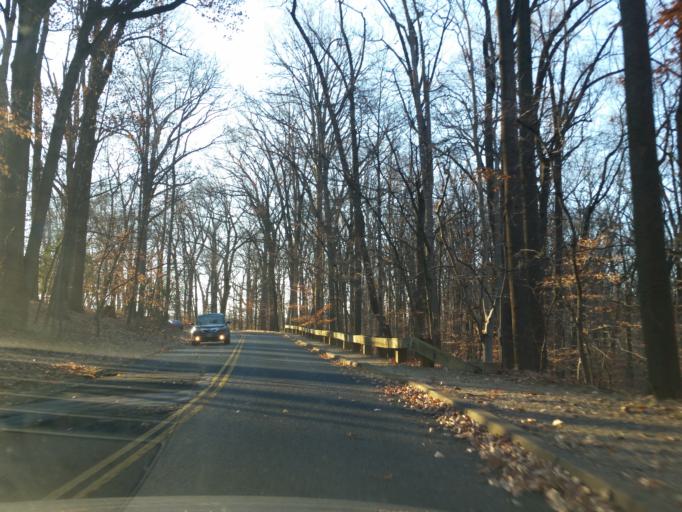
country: US
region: Maryland
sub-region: Montgomery County
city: Silver Spring
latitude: 38.9574
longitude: -77.0399
